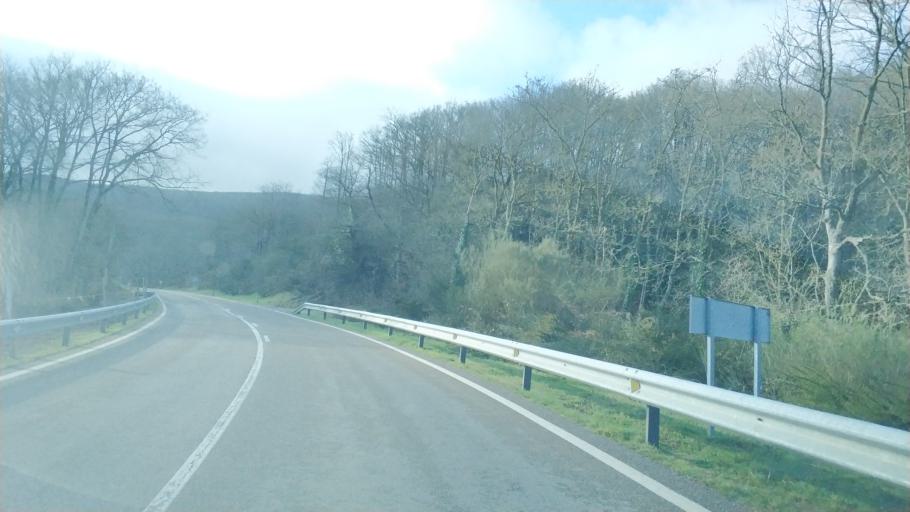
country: ES
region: Cantabria
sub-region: Provincia de Cantabria
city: Reinosa
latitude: 42.9763
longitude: -4.1029
